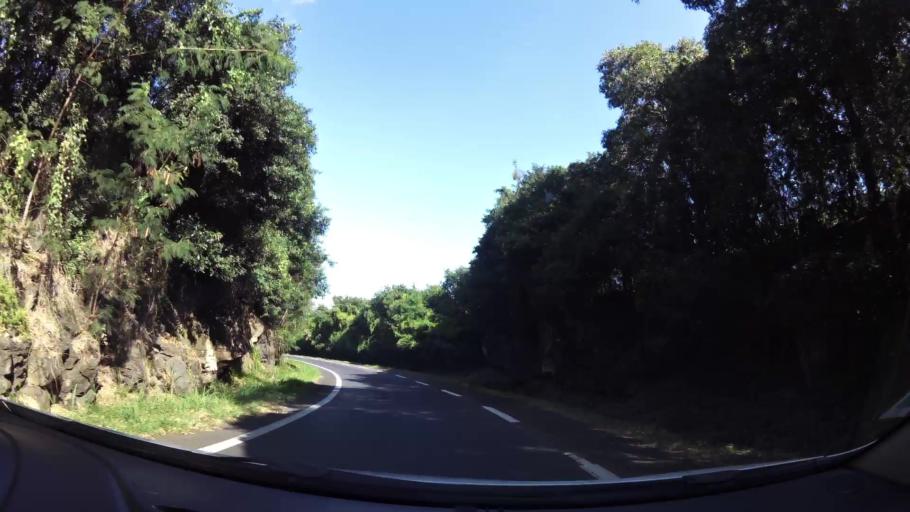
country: RE
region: Reunion
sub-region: Reunion
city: Saint-Pierre
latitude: -21.3209
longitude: 55.4881
